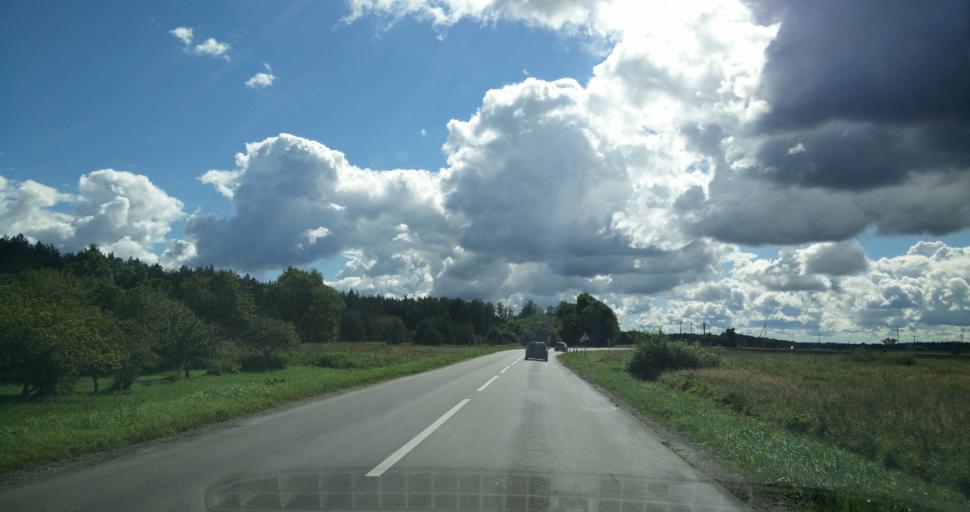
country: LT
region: Klaipedos apskritis
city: Silute
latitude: 55.3287
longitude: 21.5210
